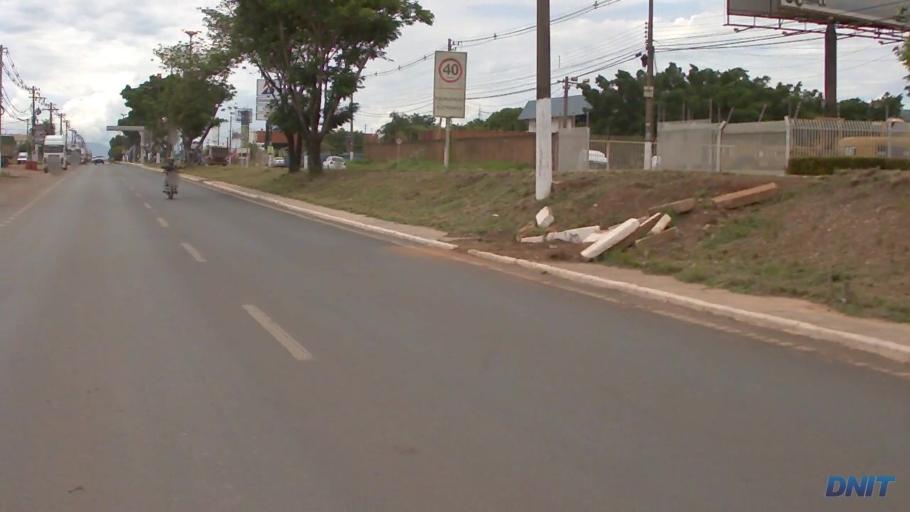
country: BR
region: Mato Grosso
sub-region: Varzea Grande
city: Varzea Grande
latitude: -15.6471
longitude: -56.1899
